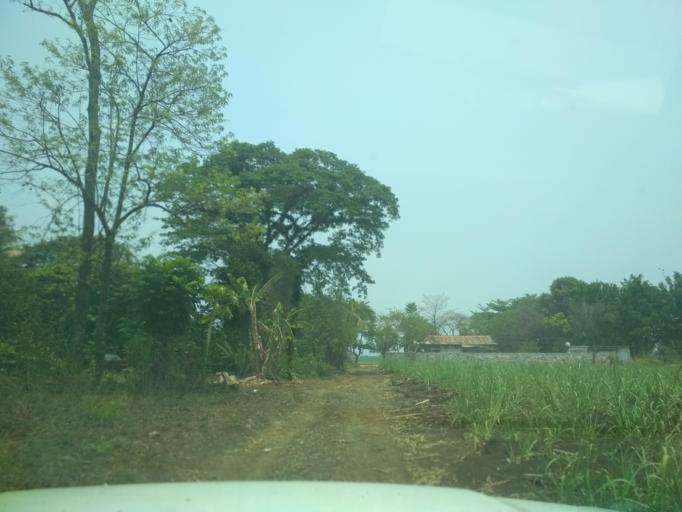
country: MX
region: Veracruz
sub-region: Tezonapa
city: Laguna Chica (Pueblo Nuevo)
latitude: 18.5114
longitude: -96.7378
